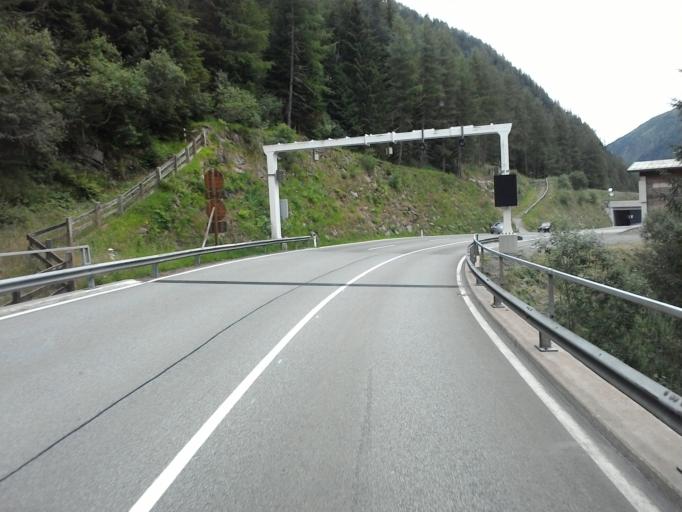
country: AT
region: Tyrol
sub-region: Politischer Bezirk Lienz
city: Matrei in Osttirol
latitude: 47.1168
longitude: 12.5059
